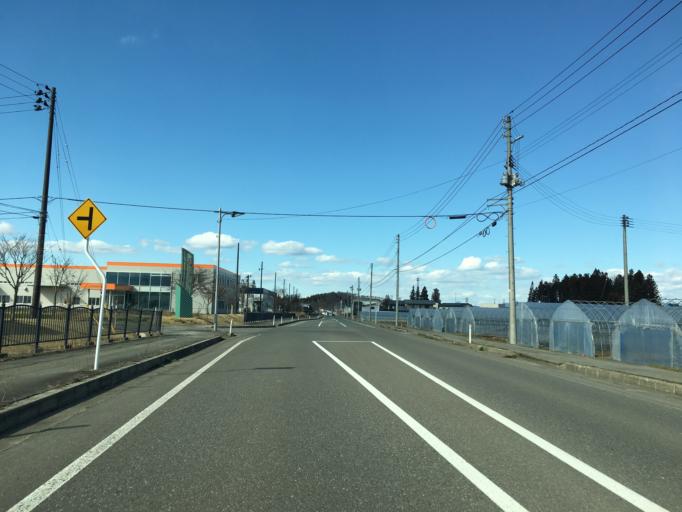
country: JP
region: Yamagata
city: Yonezawa
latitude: 37.9127
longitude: 140.1462
